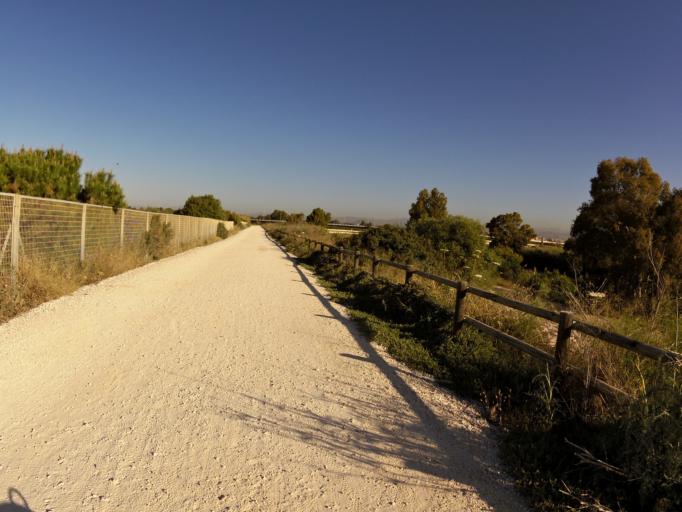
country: ES
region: Andalusia
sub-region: Provincia de Malaga
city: Torremolinos
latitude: 36.6714
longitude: -4.4619
